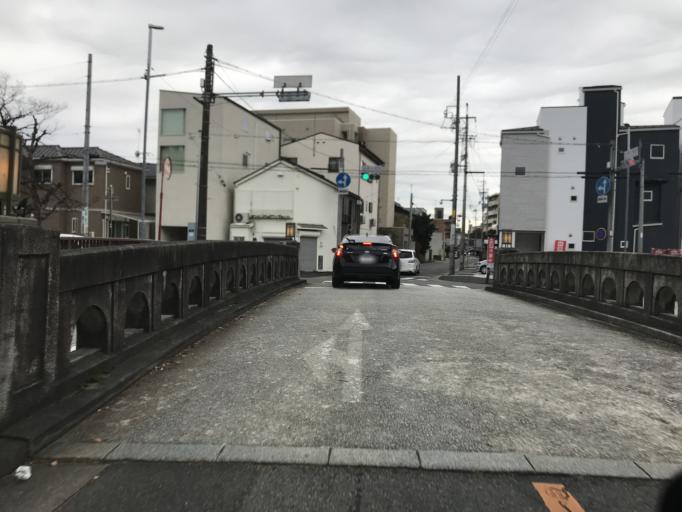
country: JP
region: Aichi
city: Nagoya-shi
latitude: 35.1908
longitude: 136.9001
